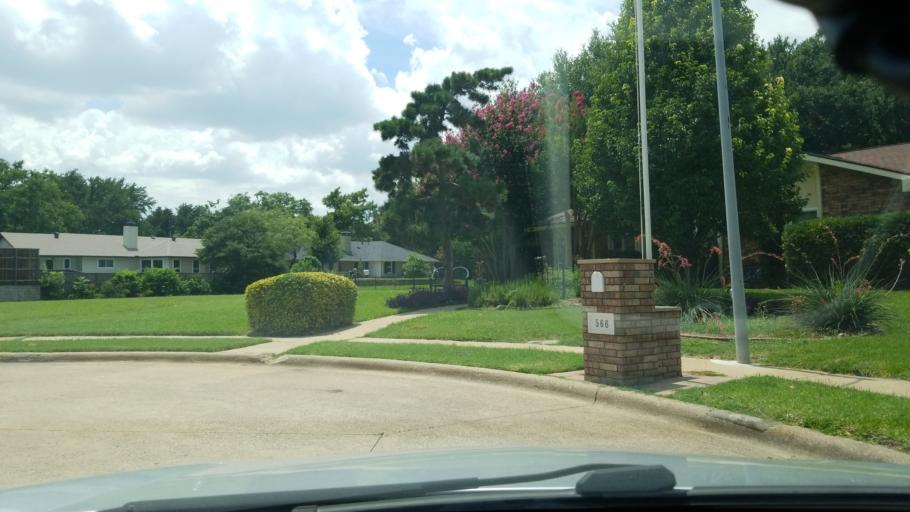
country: US
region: Texas
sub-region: Dallas County
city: Coppell
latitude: 32.9633
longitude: -96.9775
